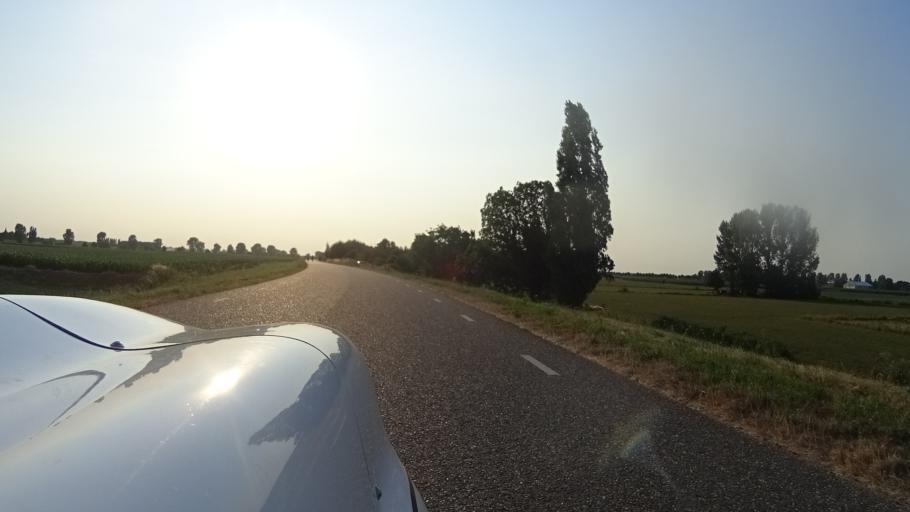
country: NL
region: Gelderland
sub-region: Gemeente Wijchen
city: Bergharen
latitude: 51.8238
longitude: 5.6260
